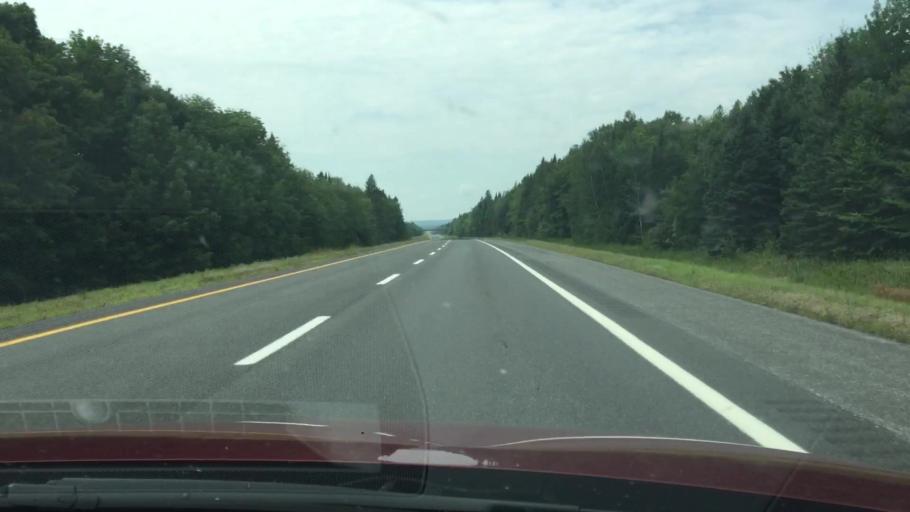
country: US
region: Maine
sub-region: Aroostook County
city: Houlton
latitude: 46.1417
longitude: -67.9422
